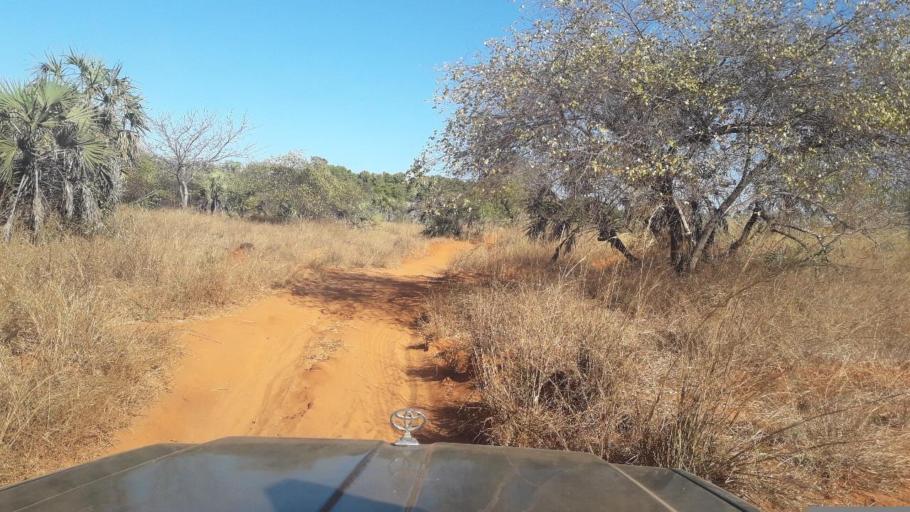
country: MG
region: Boeny
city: Sitampiky
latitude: -16.4042
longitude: 45.5982
